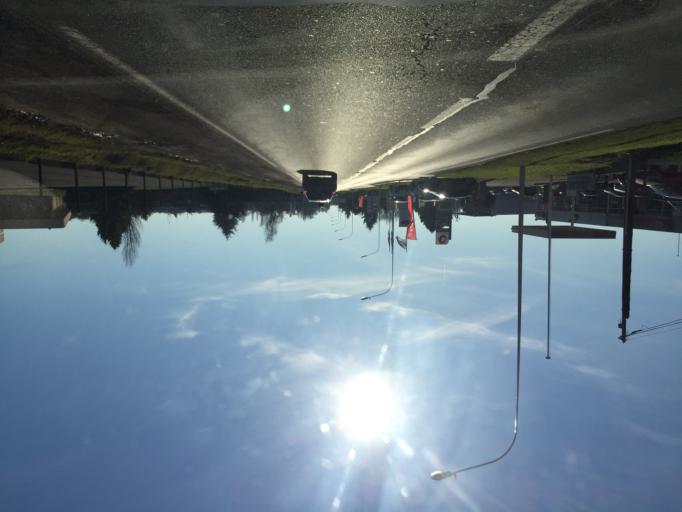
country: FR
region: Auvergne
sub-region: Departement de l'Allier
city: Saint-Remy-en-Rollat
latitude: 46.1552
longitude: 3.3933
